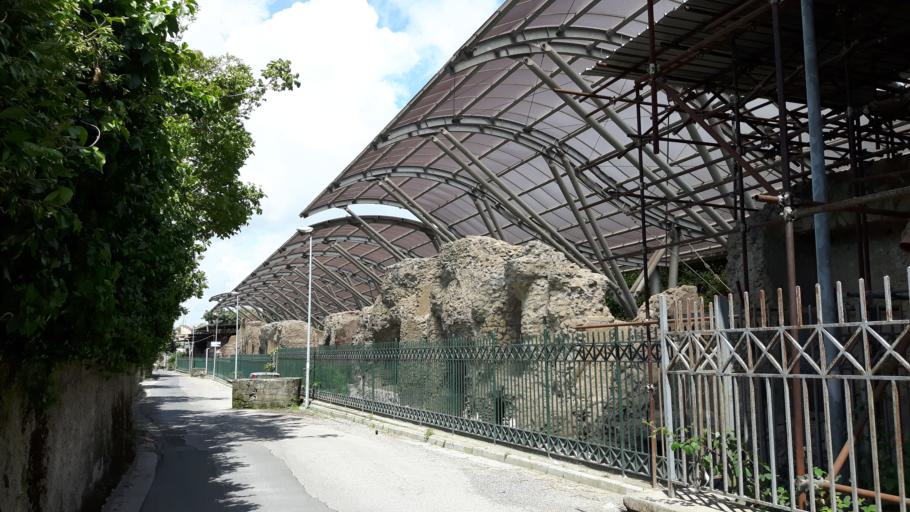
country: IT
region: Campania
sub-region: Provincia di Napoli
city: Quarto
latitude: 40.8450
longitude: 14.1192
